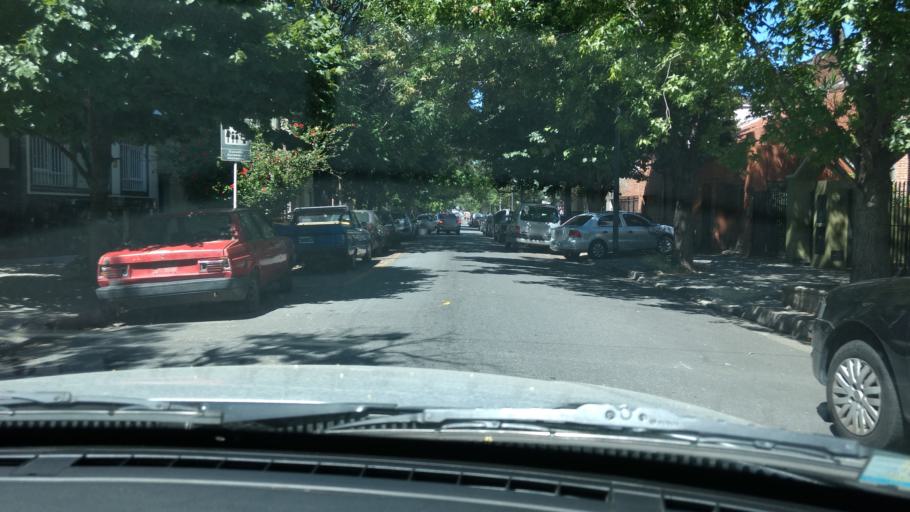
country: AR
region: Buenos Aires F.D.
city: Villa Santa Rita
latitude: -34.6194
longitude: -58.5101
